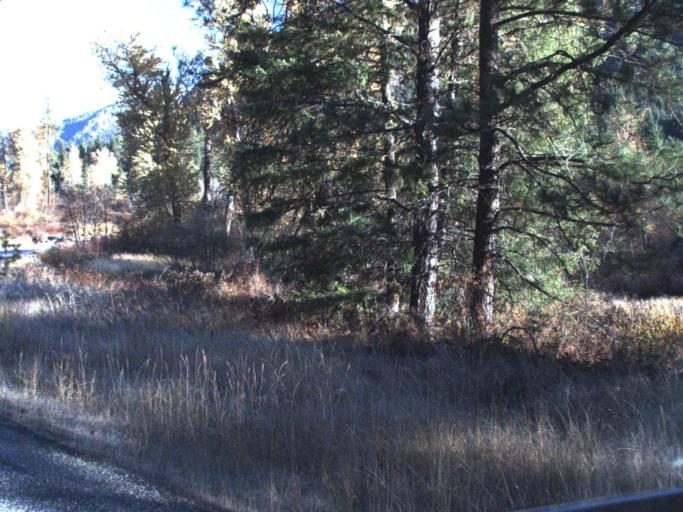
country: US
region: Washington
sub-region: Ferry County
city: Republic
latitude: 48.3270
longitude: -118.7450
